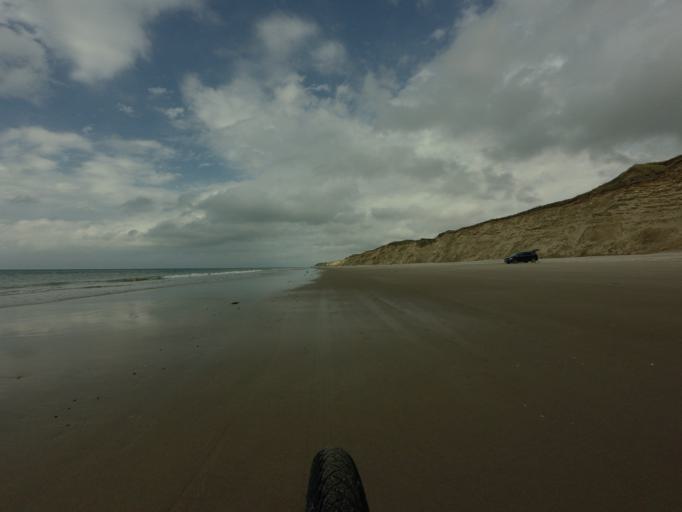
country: DK
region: North Denmark
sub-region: Jammerbugt Kommune
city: Pandrup
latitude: 57.4027
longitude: 9.7370
